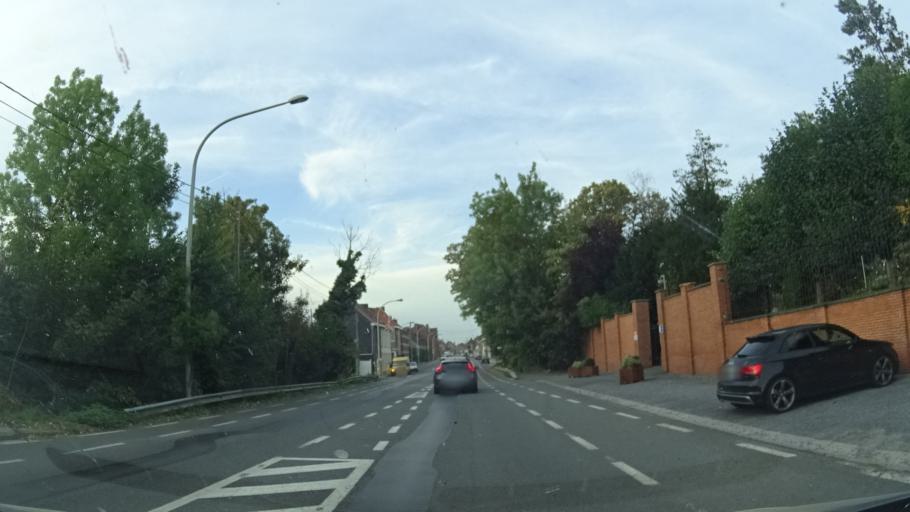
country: BE
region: Wallonia
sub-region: Province du Hainaut
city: Peruwelz
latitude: 50.5846
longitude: 3.6191
